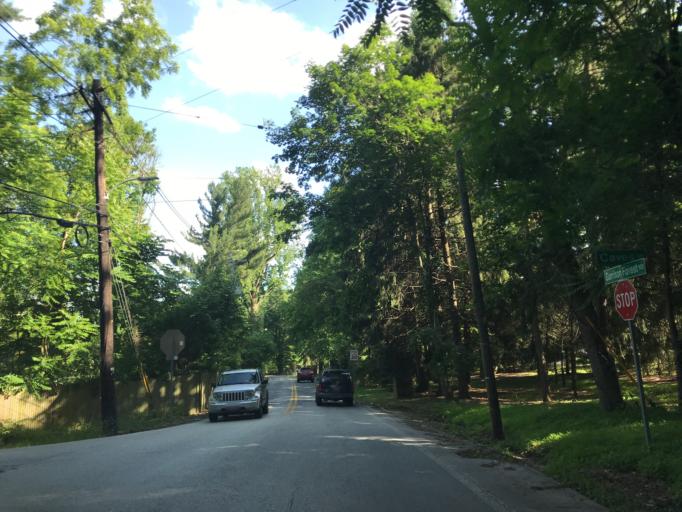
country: US
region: Maryland
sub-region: Baltimore County
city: Garrison
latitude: 39.4180
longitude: -76.7592
